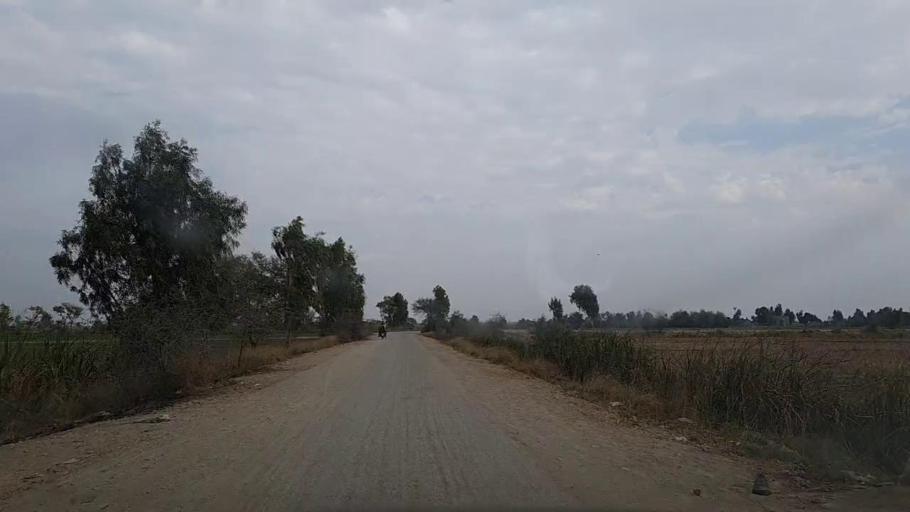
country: PK
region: Sindh
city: Sanghar
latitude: 26.2291
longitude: 69.0198
